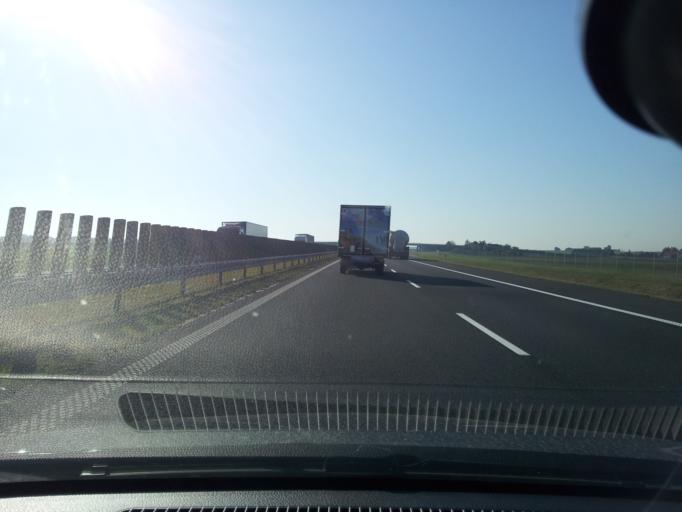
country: PL
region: Pomeranian Voivodeship
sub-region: Powiat starogardzki
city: Smetowo Graniczne
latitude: 53.7636
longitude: 18.6350
